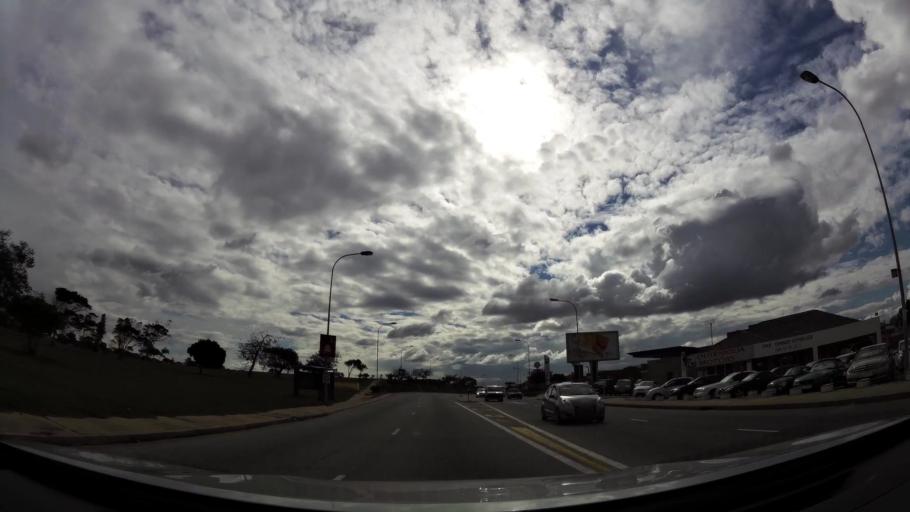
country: ZA
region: Eastern Cape
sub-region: Nelson Mandela Bay Metropolitan Municipality
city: Port Elizabeth
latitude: -33.9444
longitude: 25.5531
